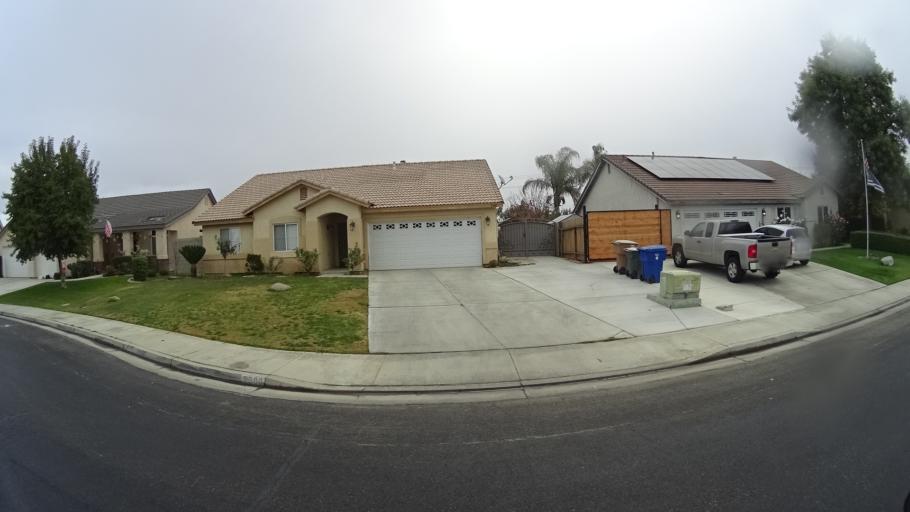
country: US
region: California
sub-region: Kern County
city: Greenfield
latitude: 35.3044
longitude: -119.0757
